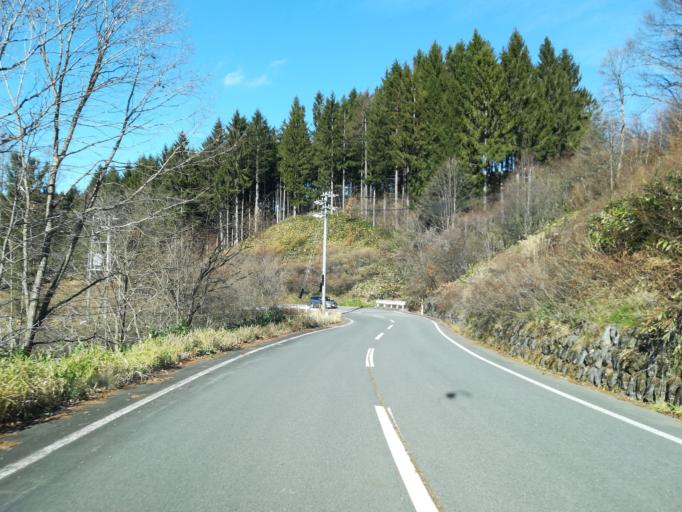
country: JP
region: Nagano
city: Ueda
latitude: 36.5176
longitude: 138.3413
